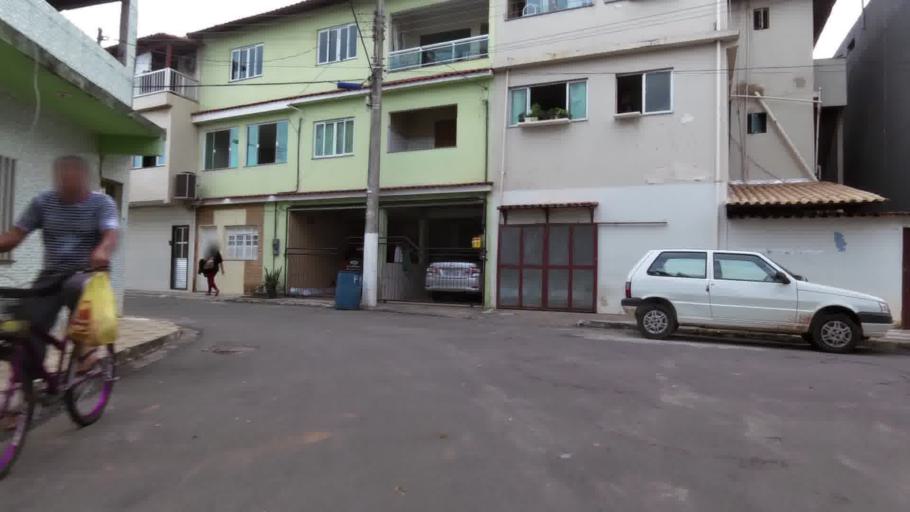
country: BR
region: Espirito Santo
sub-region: Piuma
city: Piuma
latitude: -20.8056
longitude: -40.6486
